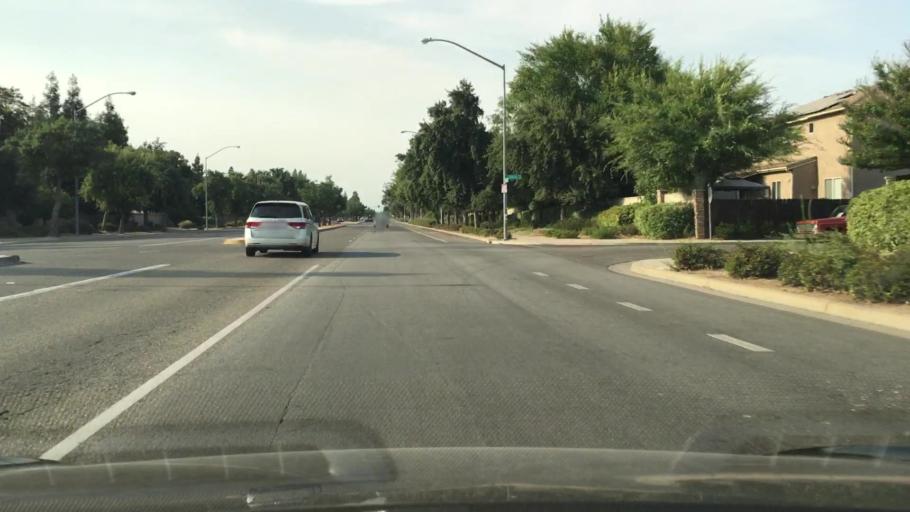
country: US
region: California
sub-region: Fresno County
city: Clovis
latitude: 36.8556
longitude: -119.7387
